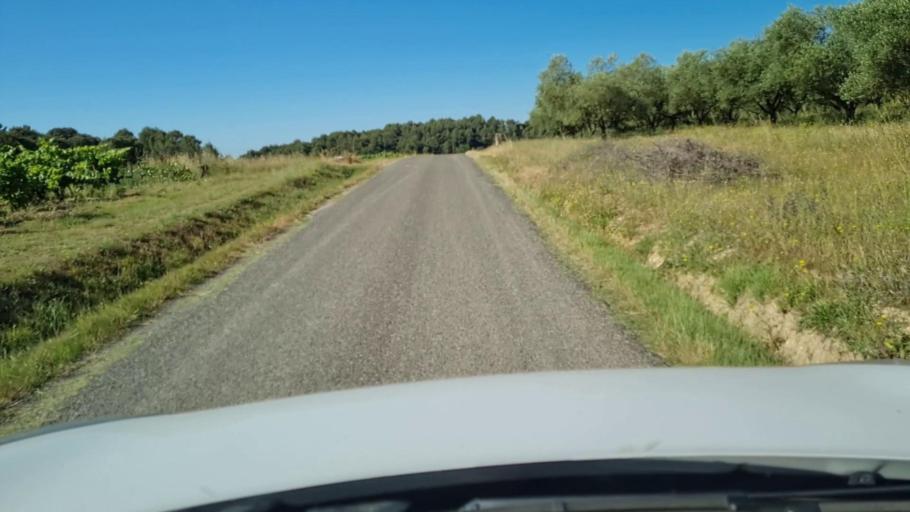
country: FR
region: Languedoc-Roussillon
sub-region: Departement du Gard
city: Sommieres
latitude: 43.8179
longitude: 4.0512
